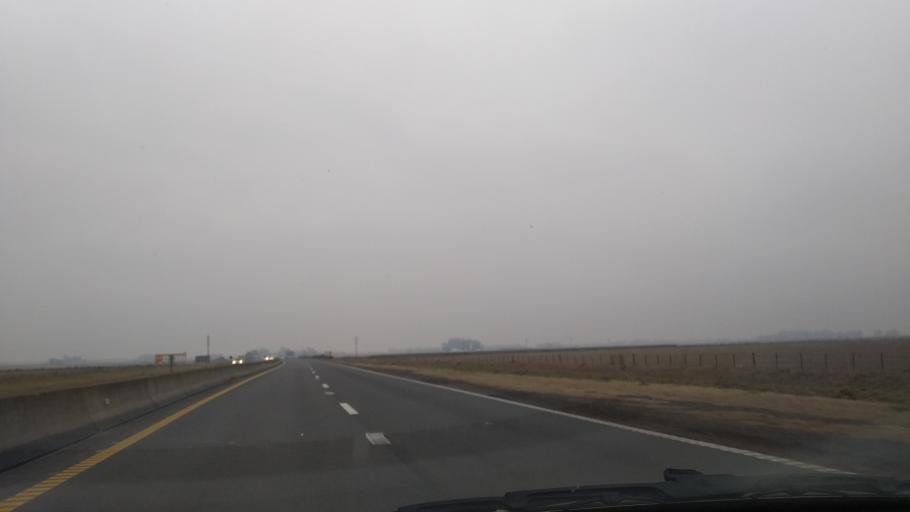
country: AR
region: Buenos Aires
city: Olavarria
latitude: -36.8557
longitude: -60.1152
